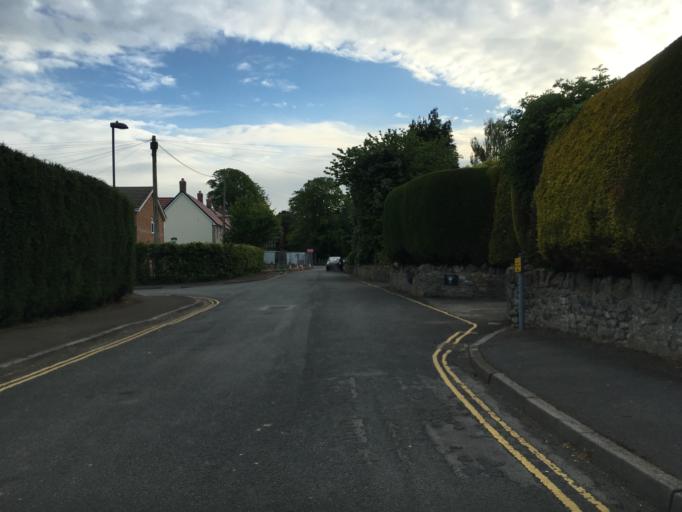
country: GB
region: England
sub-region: South Gloucestershire
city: Almondsbury
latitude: 51.5510
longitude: -2.5713
